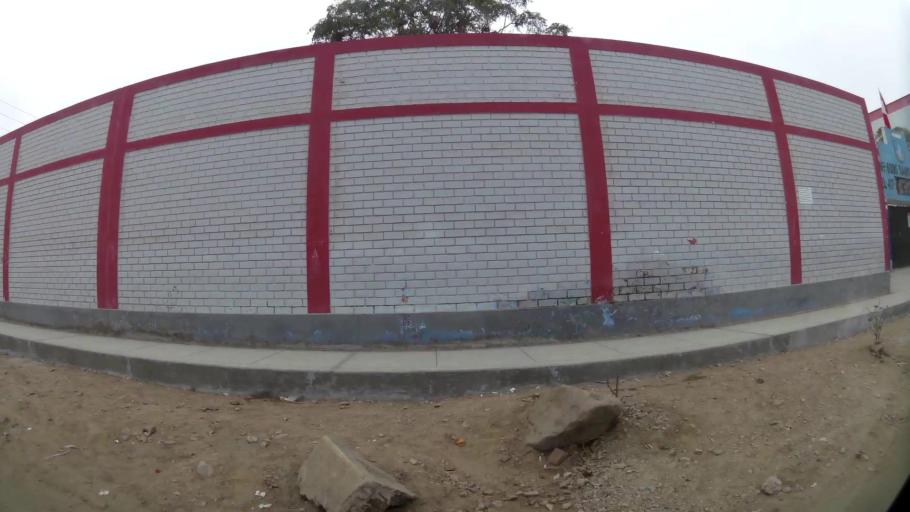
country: PE
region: Lima
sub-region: Lima
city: Surco
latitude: -12.2010
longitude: -76.9773
